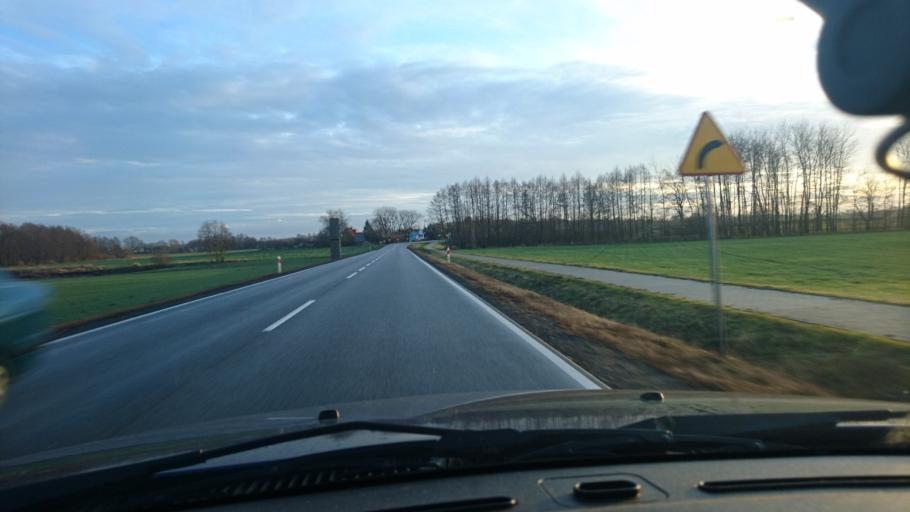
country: PL
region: Greater Poland Voivodeship
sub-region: Powiat kepinski
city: Opatow
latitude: 51.1723
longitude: 18.1458
